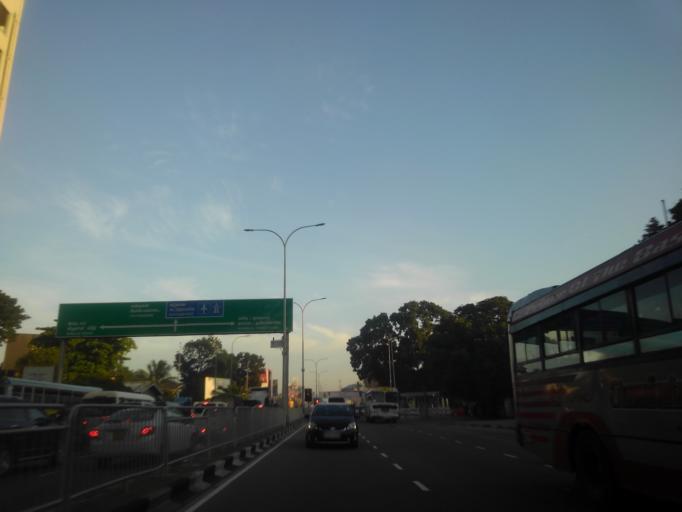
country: LK
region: Western
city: Pita Kotte
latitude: 6.8915
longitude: 79.8770
